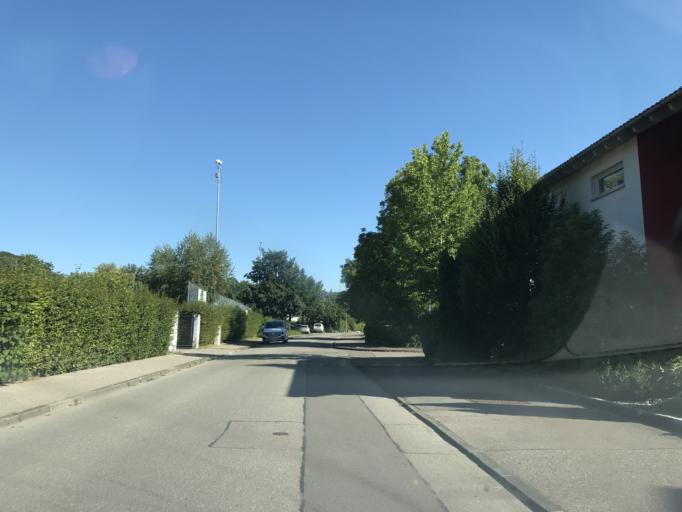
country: DE
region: Baden-Wuerttemberg
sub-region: Freiburg Region
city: Schopfheim
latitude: 47.6525
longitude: 7.8323
